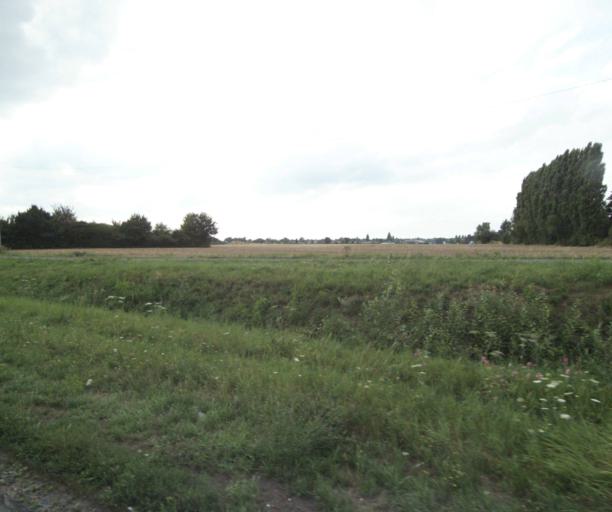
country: FR
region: Nord-Pas-de-Calais
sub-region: Departement du Nord
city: Sailly-lez-Lannoy
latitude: 50.6569
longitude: 3.2115
